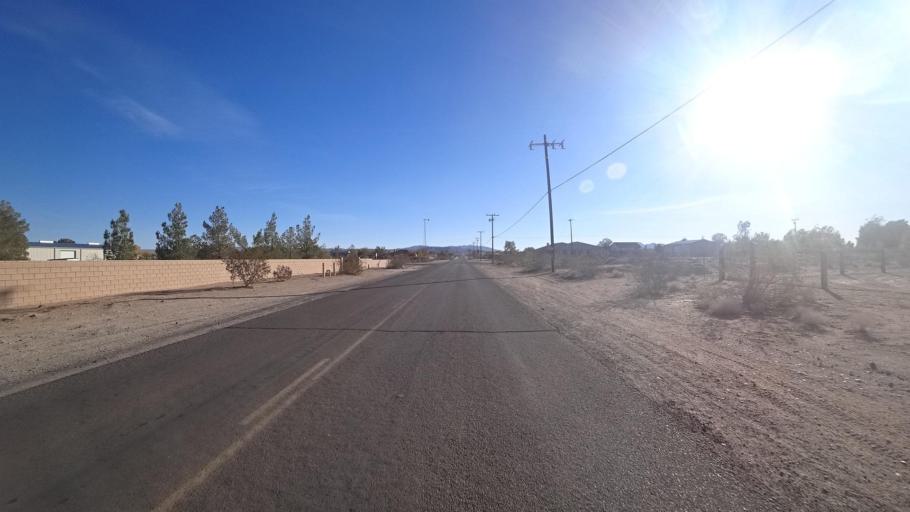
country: US
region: California
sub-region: Kern County
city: Ridgecrest
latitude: 35.6381
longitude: -117.7055
